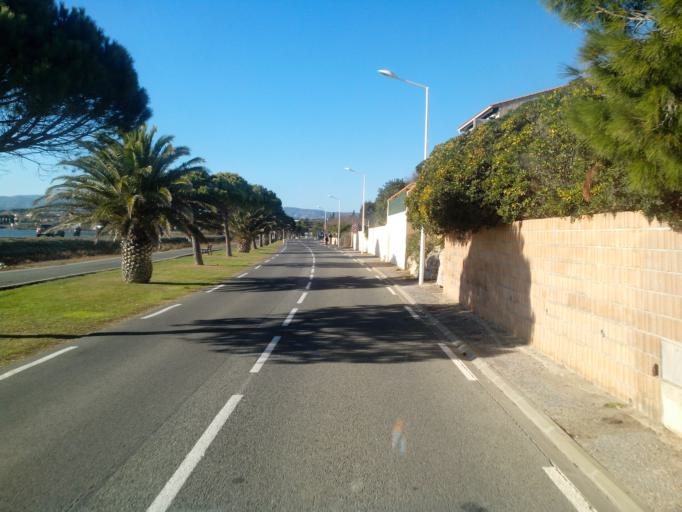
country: FR
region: Languedoc-Roussillon
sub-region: Departement de l'Aude
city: Leucate
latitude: 42.9045
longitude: 3.0459
